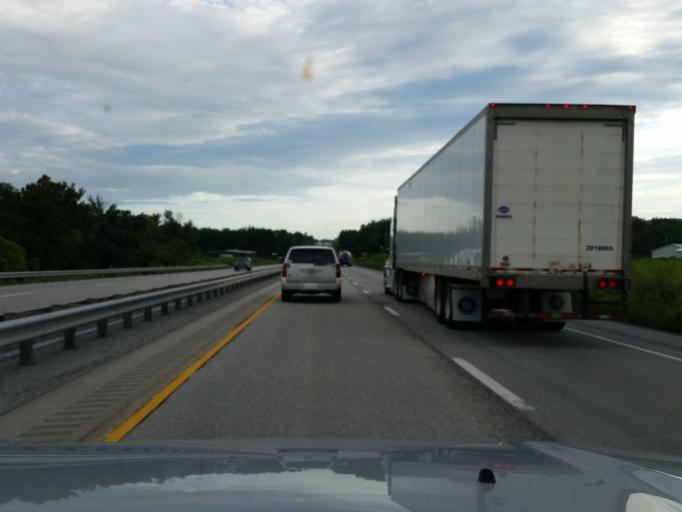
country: US
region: Pennsylvania
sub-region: Adams County
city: Lake Meade
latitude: 40.0315
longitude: -77.0822
